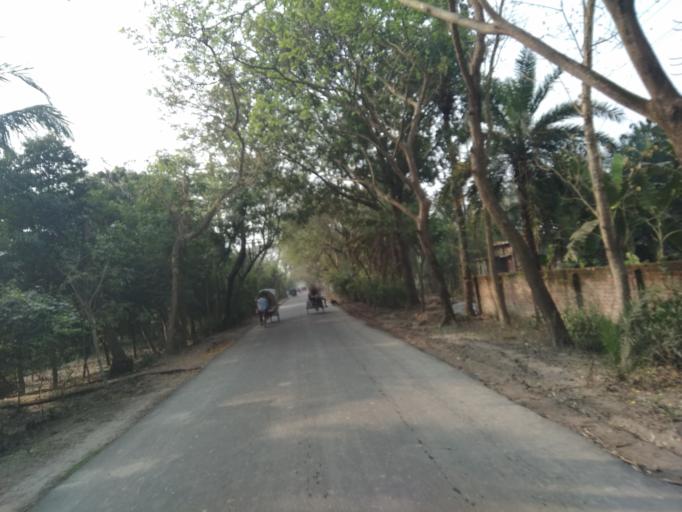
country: IN
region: West Bengal
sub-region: North 24 Parganas
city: Taki
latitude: 22.3241
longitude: 89.1057
